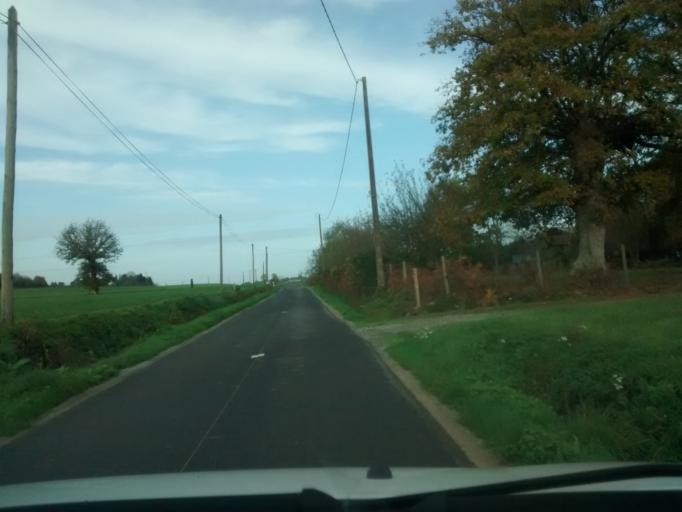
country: FR
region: Brittany
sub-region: Departement d'Ille-et-Vilaine
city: Brece
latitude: 48.1141
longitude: -1.4882
